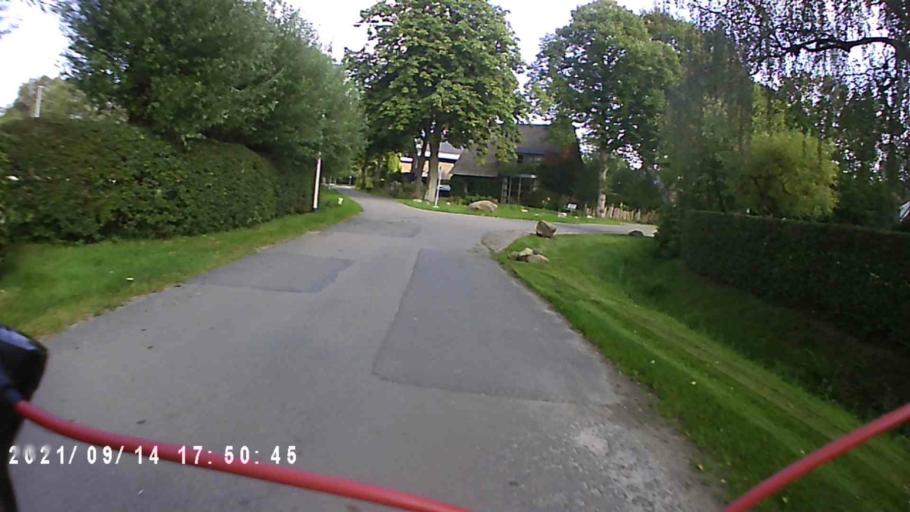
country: NL
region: Groningen
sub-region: Gemeente Haren
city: Haren
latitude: 53.1365
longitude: 6.6257
